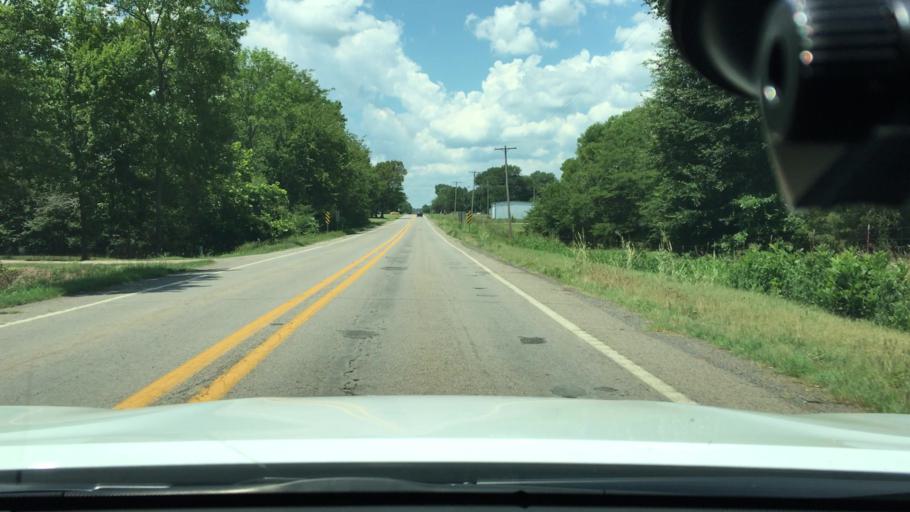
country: US
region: Arkansas
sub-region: Logan County
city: Booneville
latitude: 35.1475
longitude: -93.8484
